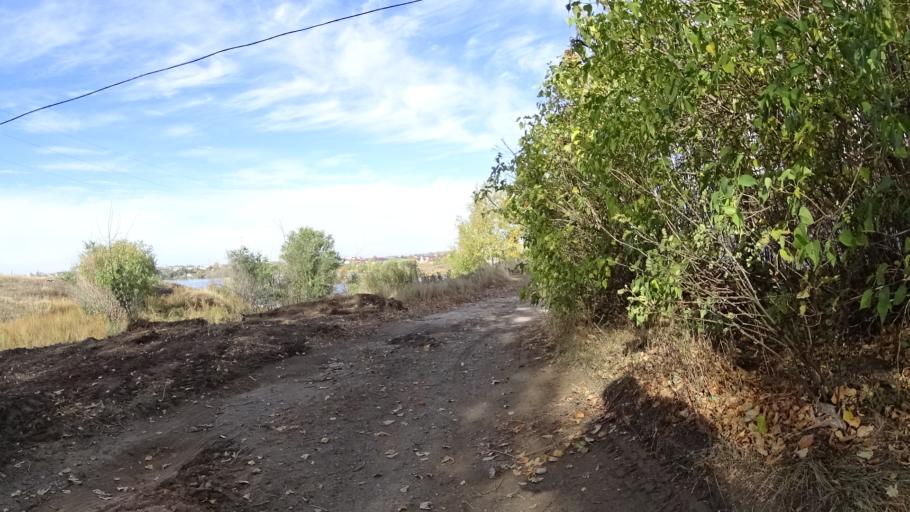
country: RU
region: Chelyabinsk
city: Troitsk
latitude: 54.0793
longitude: 61.5817
